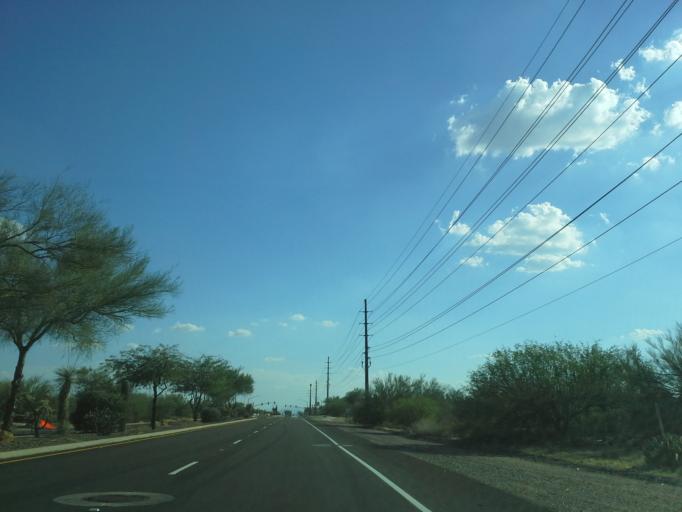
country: US
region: Arizona
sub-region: Maricopa County
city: Cave Creek
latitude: 33.8028
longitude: -111.9616
